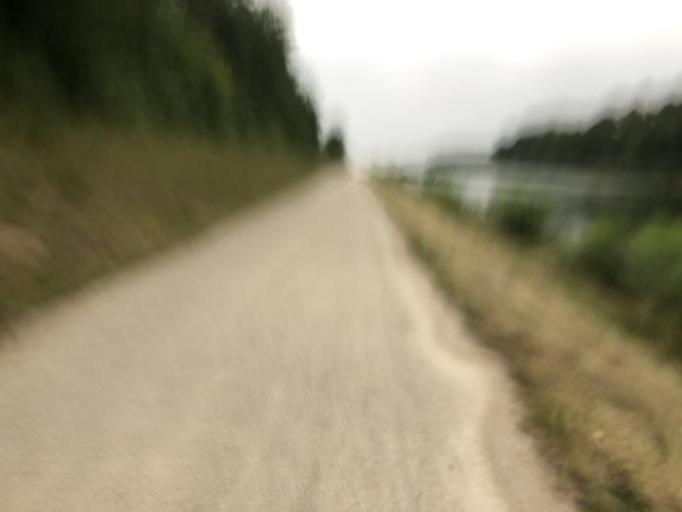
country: DE
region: Bavaria
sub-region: Regierungsbezirk Mittelfranken
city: Erlangen
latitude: 49.5436
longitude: 10.9691
